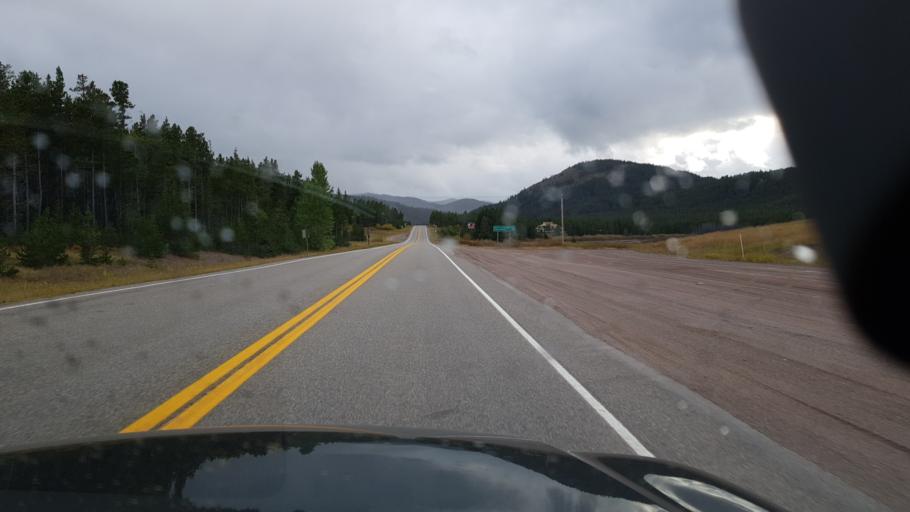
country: US
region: Montana
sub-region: Glacier County
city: South Browning
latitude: 48.3170
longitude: -113.3543
